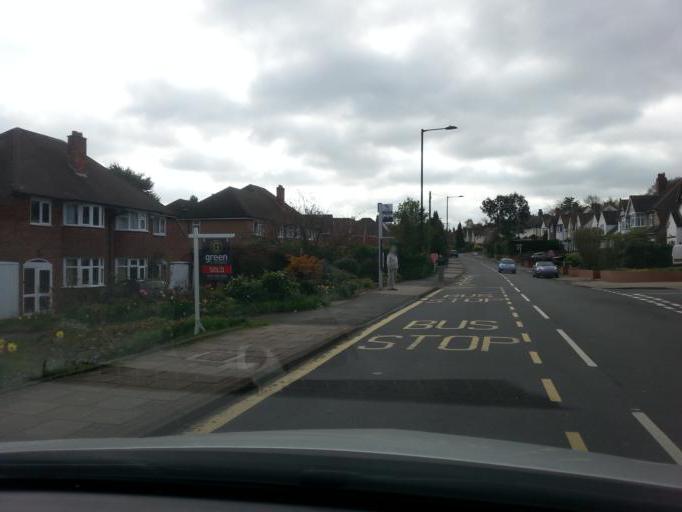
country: GB
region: England
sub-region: City and Borough of Birmingham
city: Sutton Coldfield
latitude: 52.5892
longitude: -1.8394
